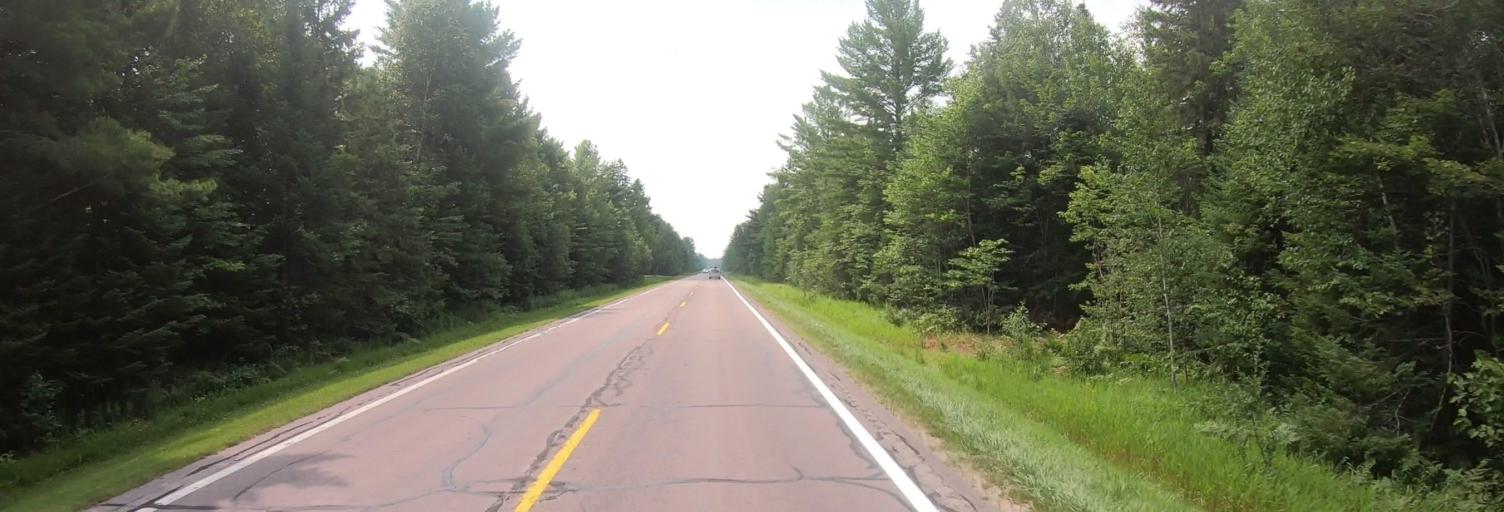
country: US
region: Michigan
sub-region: Luce County
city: Newberry
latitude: 46.4840
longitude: -85.4269
